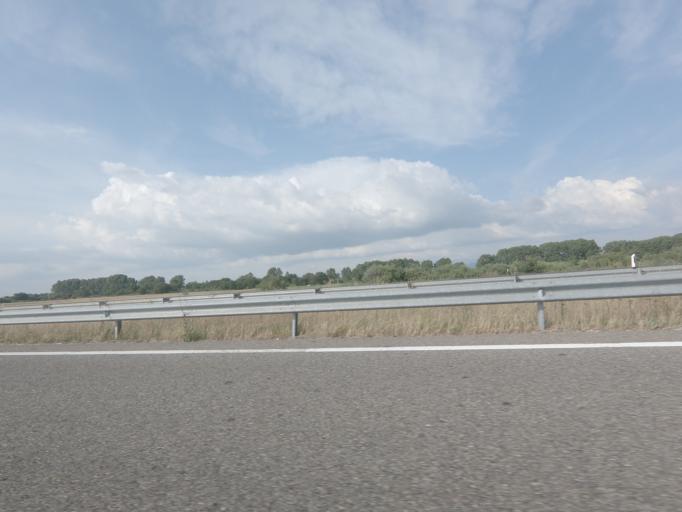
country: ES
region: Galicia
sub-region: Provincia de Ourense
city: Xinzo de Limia
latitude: 42.0830
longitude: -7.7162
